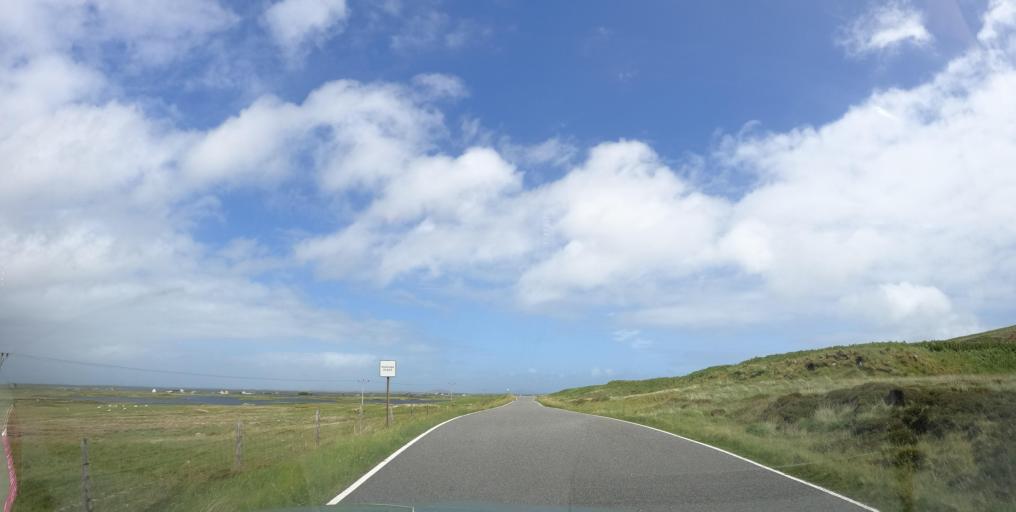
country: GB
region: Scotland
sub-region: Eilean Siar
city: Isle of South Uist
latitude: 57.3444
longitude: -7.3640
